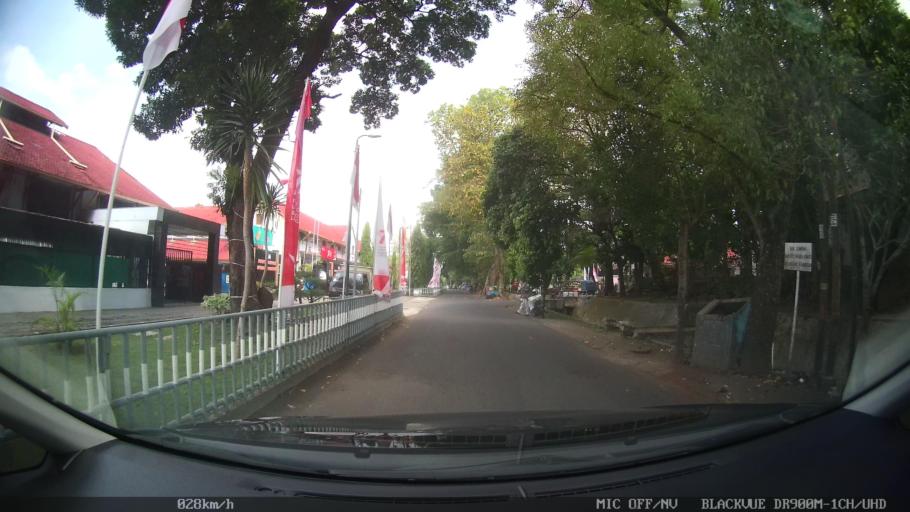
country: ID
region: Daerah Istimewa Yogyakarta
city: Yogyakarta
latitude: -7.7870
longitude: 110.3845
